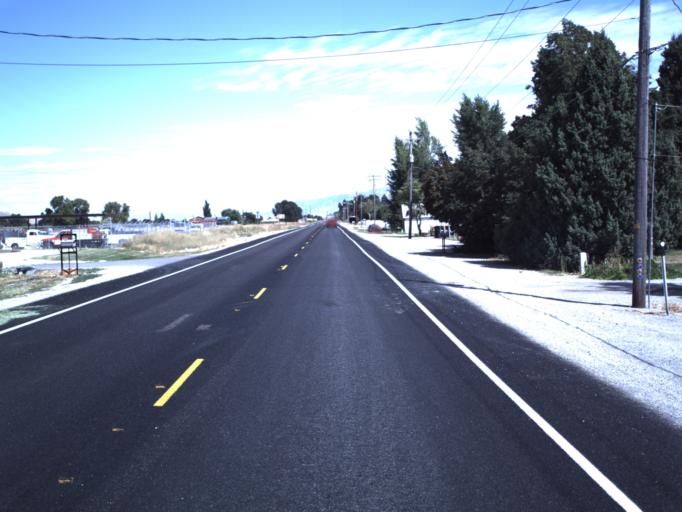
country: US
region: Utah
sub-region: Box Elder County
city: Tremonton
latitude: 41.7157
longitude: -112.1424
